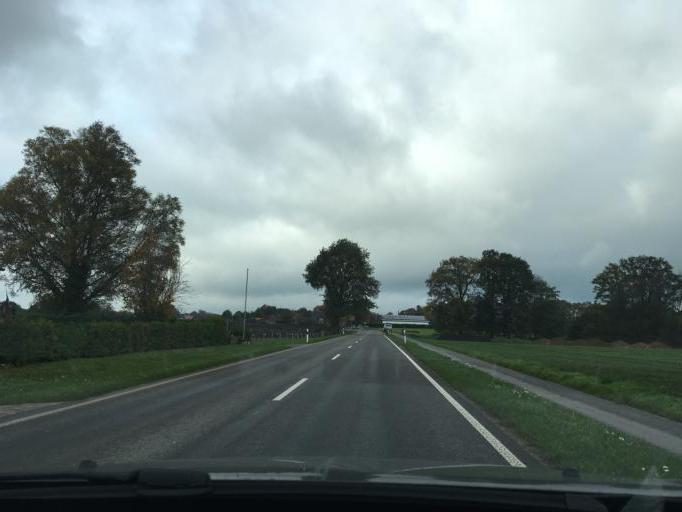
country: NL
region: Overijssel
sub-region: Gemeente Haaksbergen
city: Haaksbergen
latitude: 52.0945
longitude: 6.7638
